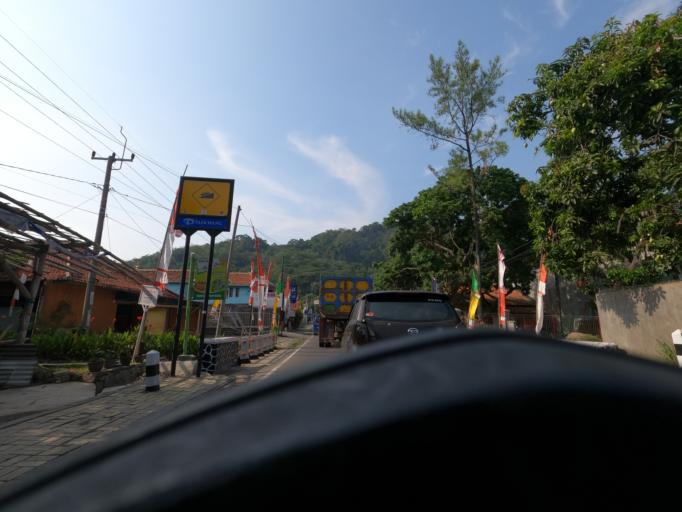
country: ID
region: West Java
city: Lembang
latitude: -6.6302
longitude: 107.7211
